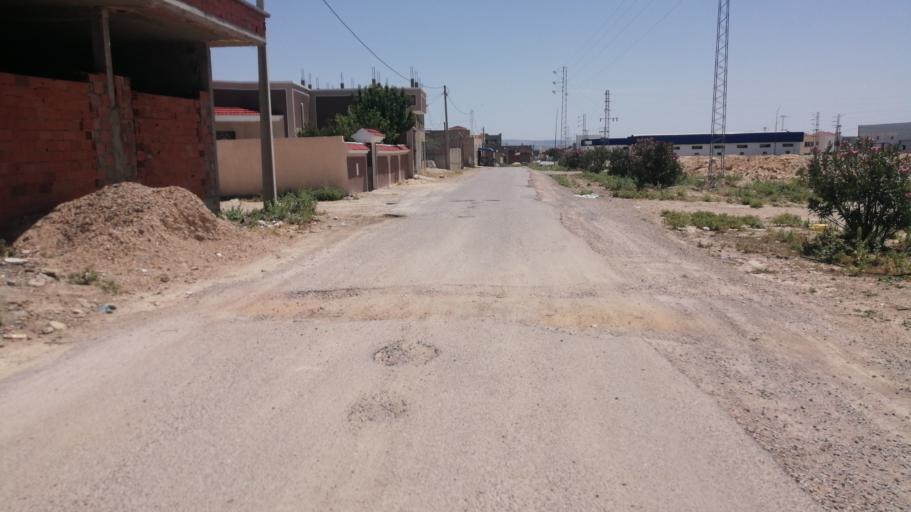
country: TN
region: Silyanah
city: Maktar
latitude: 35.8520
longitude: 9.1967
